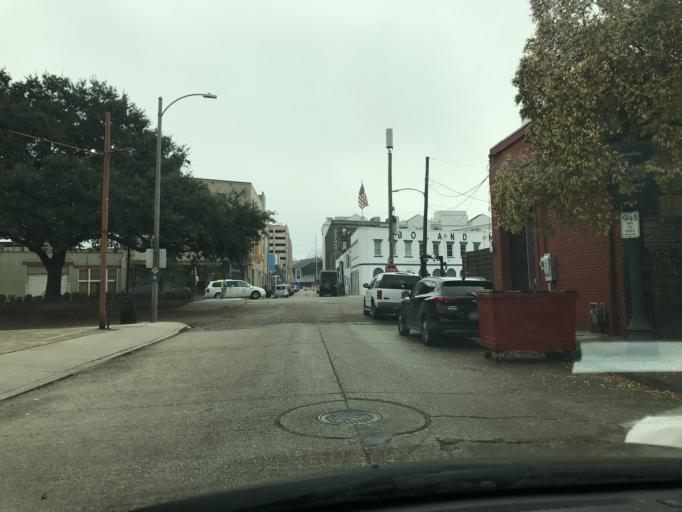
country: US
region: Louisiana
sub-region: Orleans Parish
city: New Orleans
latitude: 29.9423
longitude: -90.0680
